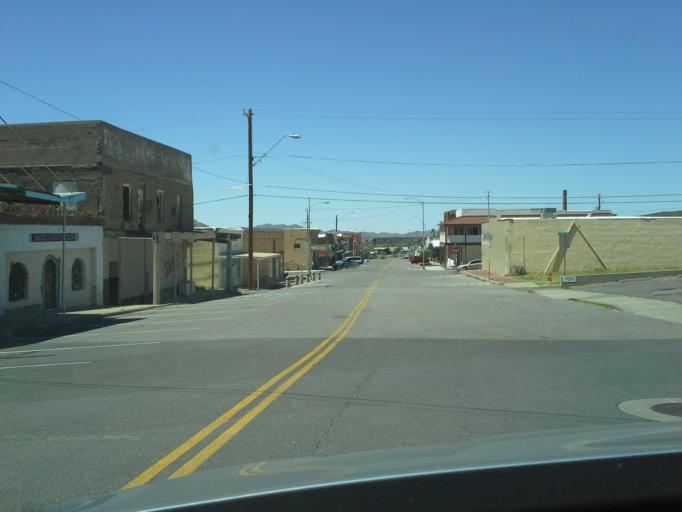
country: US
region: Arizona
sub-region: Pinal County
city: Superior
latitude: 33.2940
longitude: -111.0953
